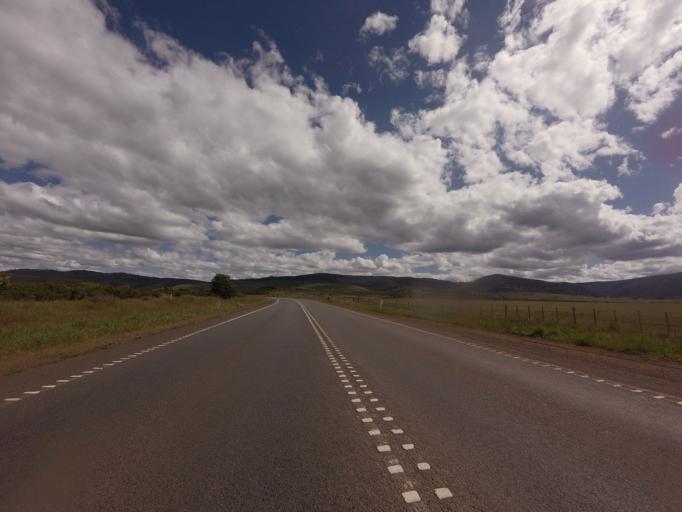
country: AU
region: Tasmania
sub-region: Brighton
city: Bridgewater
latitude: -42.1785
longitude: 147.3872
